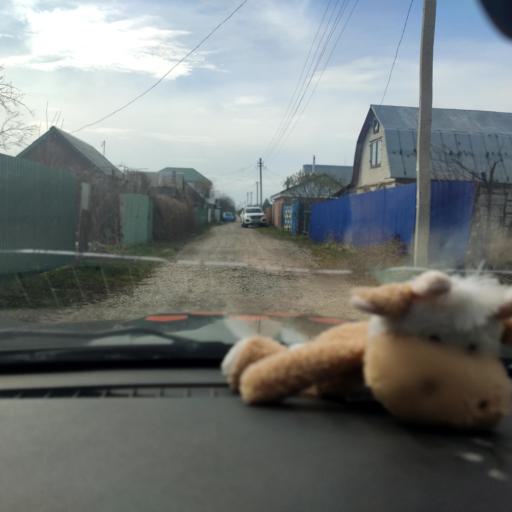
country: RU
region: Samara
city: Podstepki
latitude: 53.5944
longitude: 49.2352
